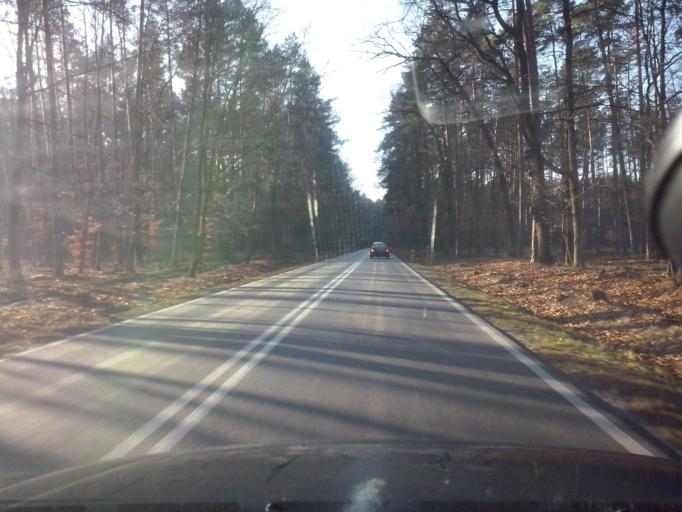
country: PL
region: Subcarpathian Voivodeship
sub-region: Powiat nizanski
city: Bieliny
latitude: 50.3952
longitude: 22.2824
